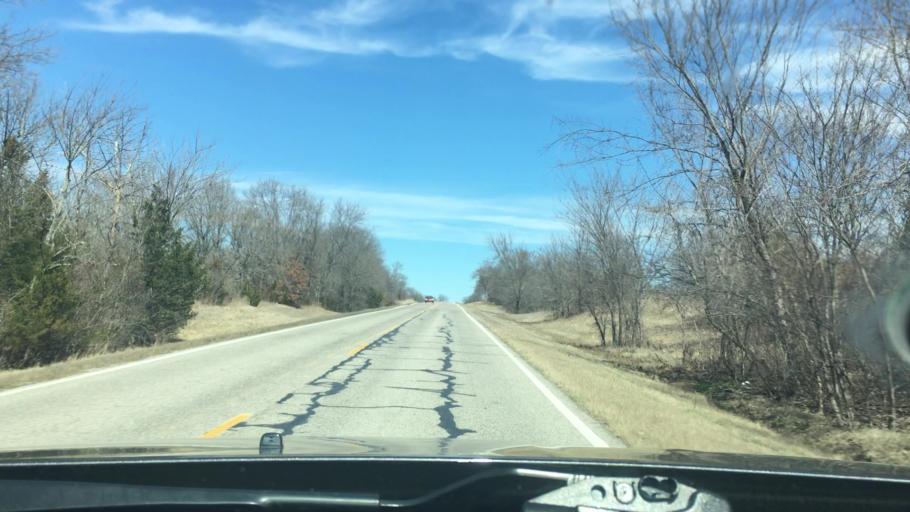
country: US
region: Oklahoma
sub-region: Carter County
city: Dickson
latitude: 34.3152
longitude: -96.9618
